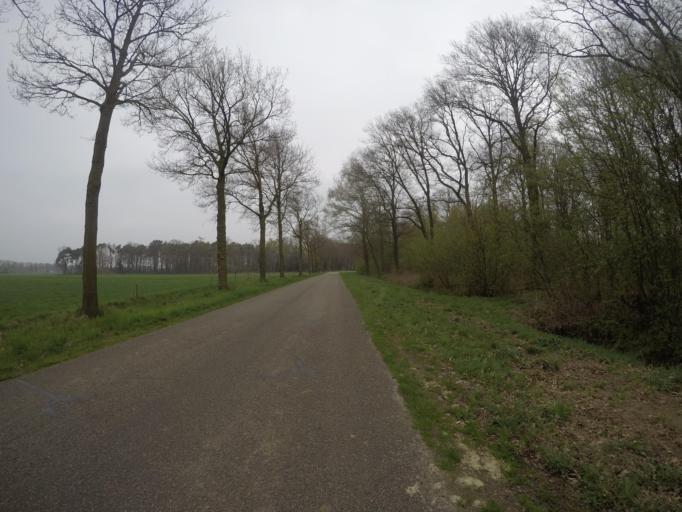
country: NL
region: Gelderland
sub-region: Gemeente Aalten
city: Aalten
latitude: 51.8894
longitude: 6.5645
